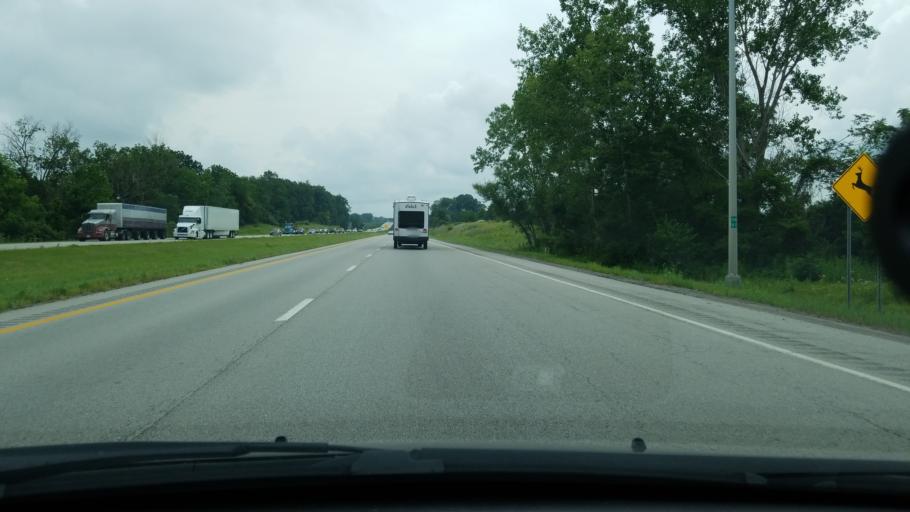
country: US
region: Ohio
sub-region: Erie County
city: Huron
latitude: 41.3699
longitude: -82.5617
